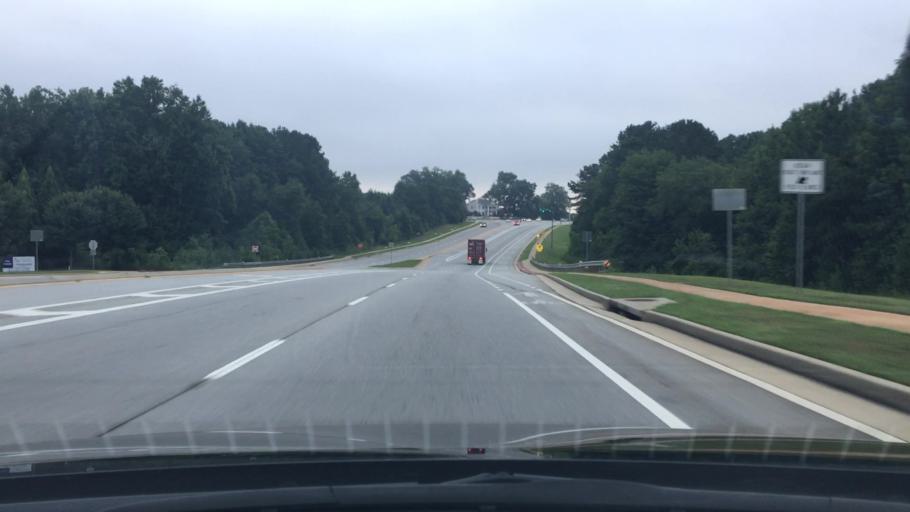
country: US
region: Georgia
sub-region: Coweta County
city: Senoia
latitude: 33.3422
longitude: -84.5301
